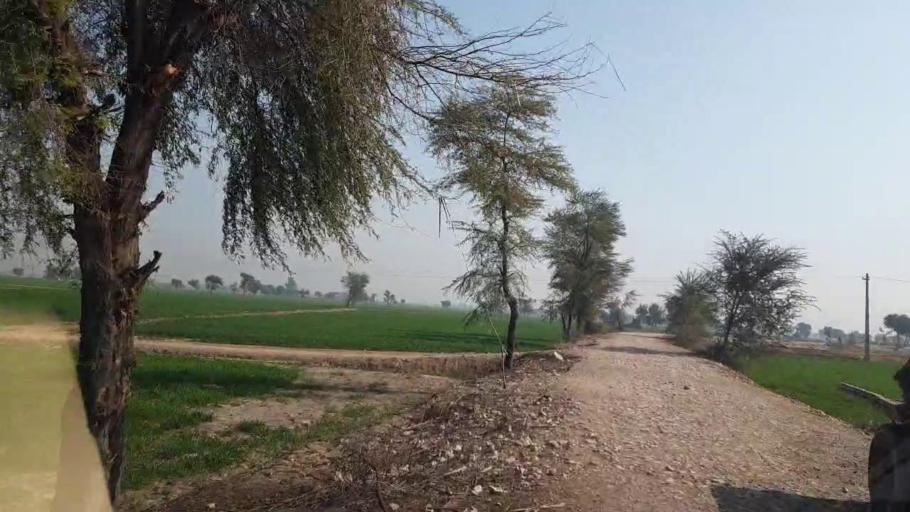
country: PK
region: Sindh
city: Ubauro
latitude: 28.1144
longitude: 69.7881
